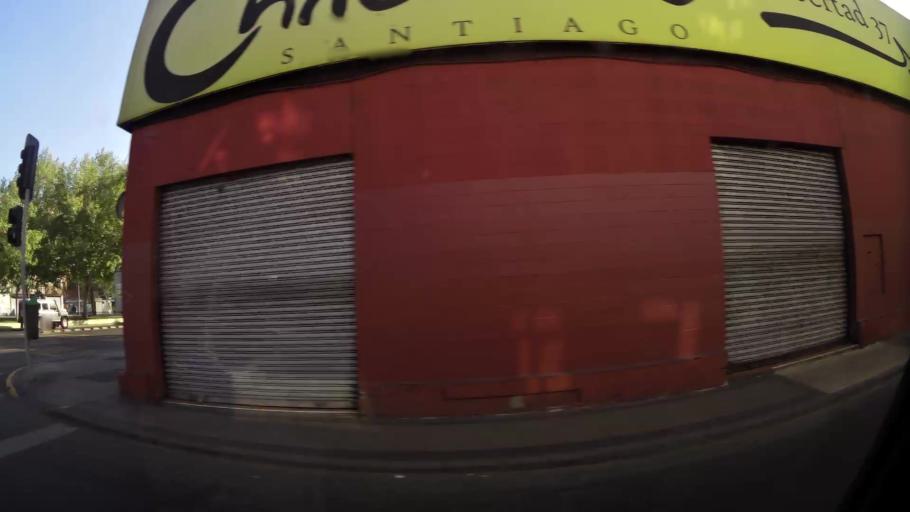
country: CL
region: Santiago Metropolitan
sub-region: Provincia de Santiago
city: Santiago
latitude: -33.4491
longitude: -70.6730
